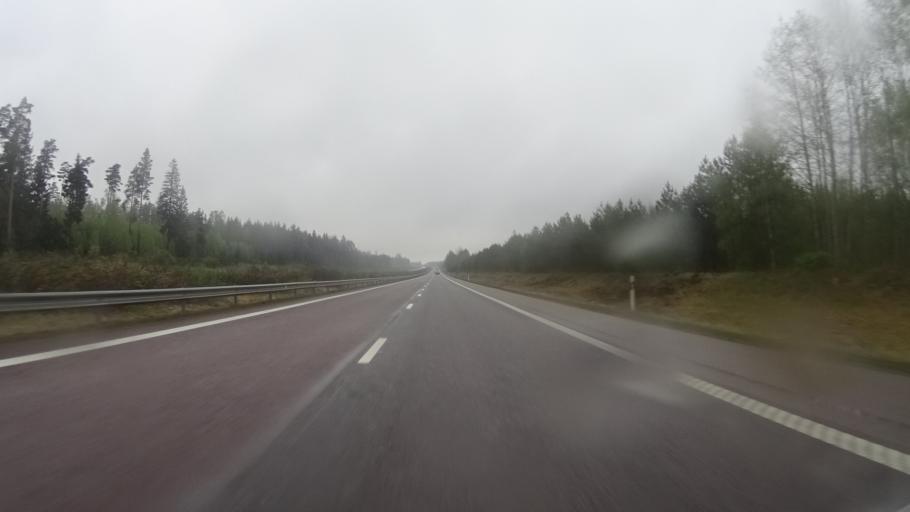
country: SE
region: Kronoberg
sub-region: Markaryds Kommun
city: Stromsnasbruk
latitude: 56.6667
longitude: 13.8190
